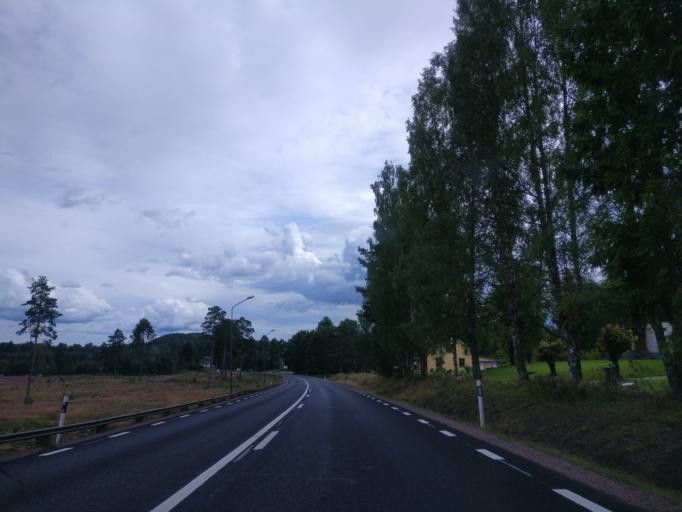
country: SE
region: Vaermland
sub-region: Hagfors Kommun
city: Ekshaerad
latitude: 60.0668
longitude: 13.5490
